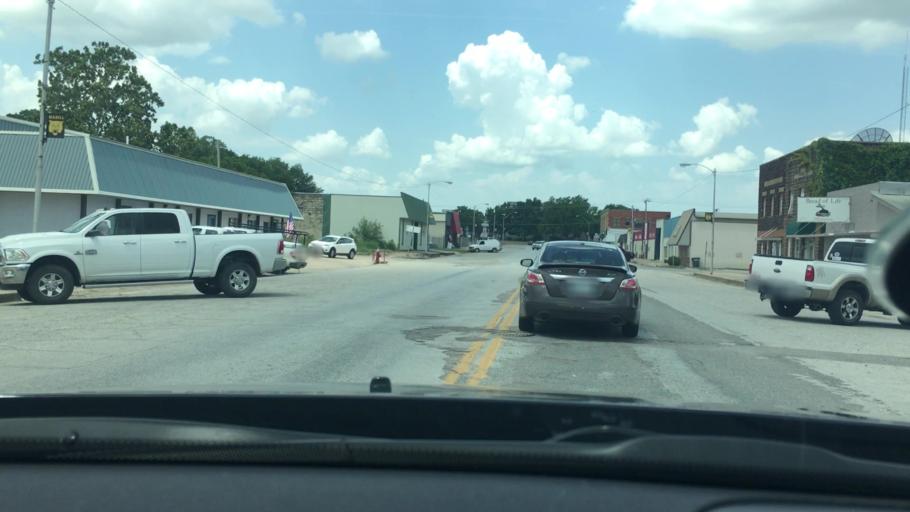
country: US
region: Oklahoma
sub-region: Marshall County
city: Madill
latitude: 34.0918
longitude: -96.7673
